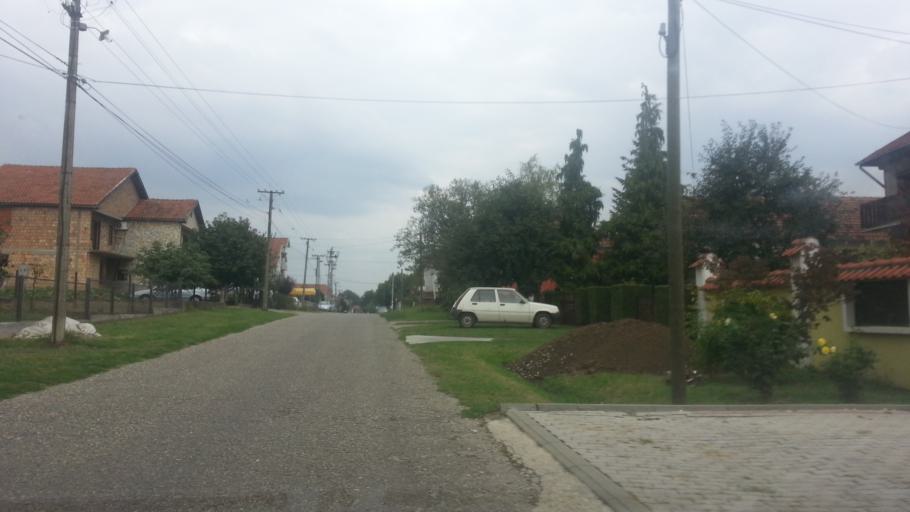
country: RS
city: Stari Banovci
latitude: 44.9772
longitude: 20.2776
